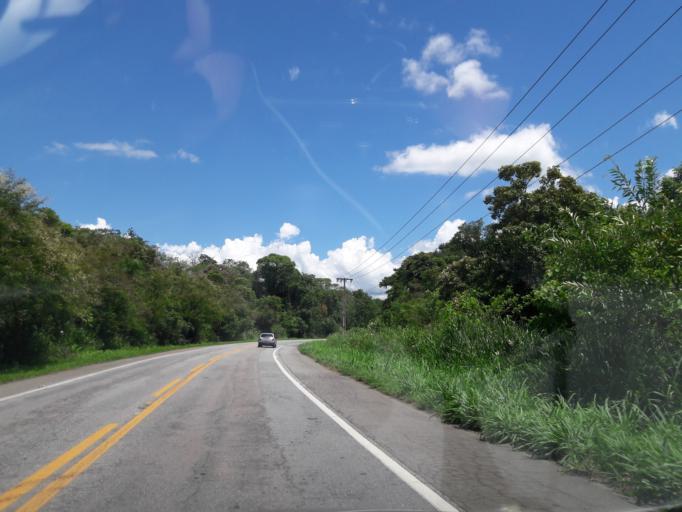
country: BR
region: Parana
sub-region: Antonina
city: Antonina
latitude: -25.4474
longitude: -48.7988
